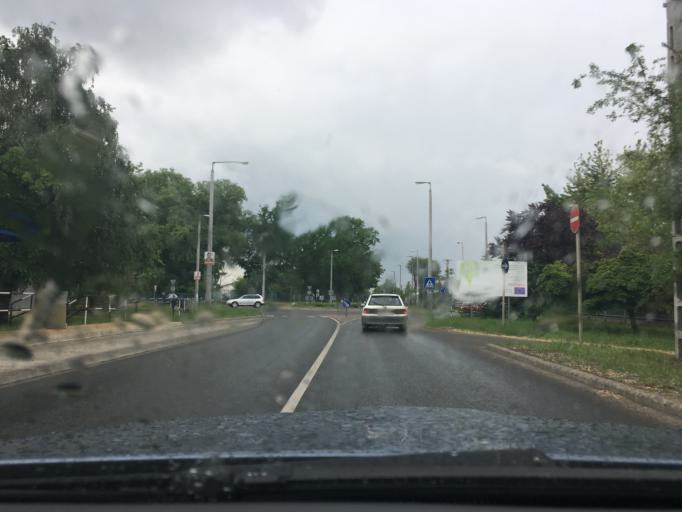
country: HU
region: Hajdu-Bihar
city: Debrecen
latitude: 47.5160
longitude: 21.6568
